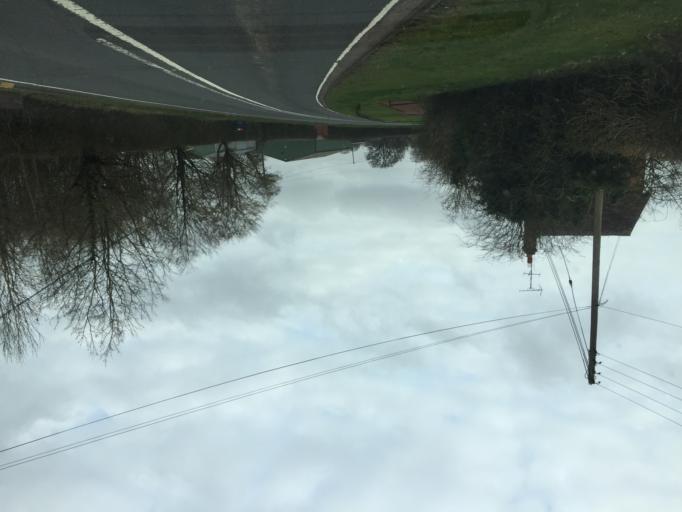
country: GB
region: England
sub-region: Warwickshire
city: Henley in Arden
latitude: 52.3010
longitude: -1.8346
